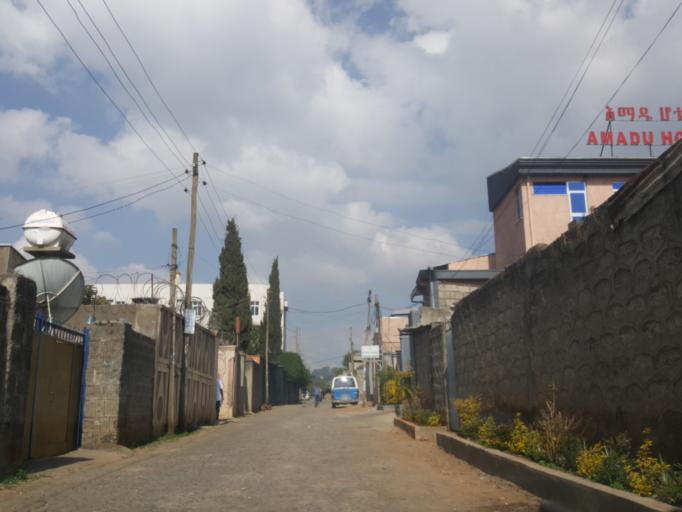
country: ET
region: Adis Abeba
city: Addis Ababa
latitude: 9.0544
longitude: 38.7194
